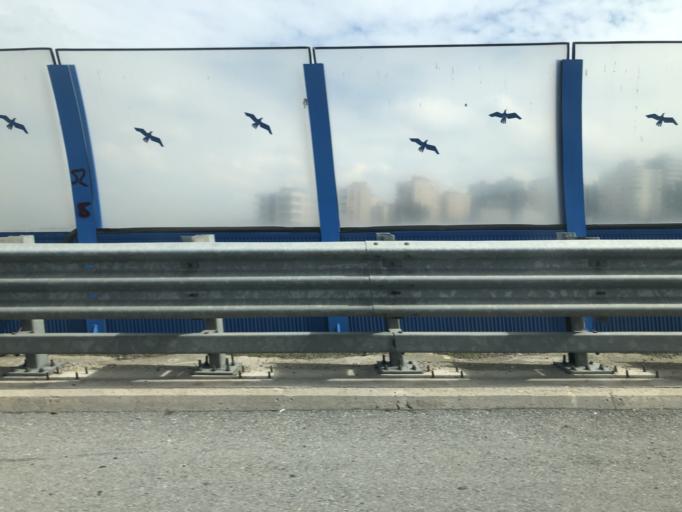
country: TR
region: Izmir
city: Karabaglar
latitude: 38.3932
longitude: 27.0628
